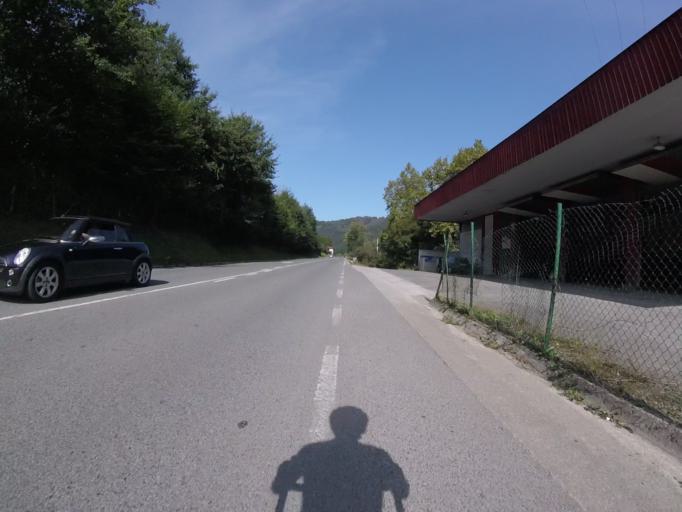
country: ES
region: Navarre
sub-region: Provincia de Navarra
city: Doneztebe
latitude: 43.1380
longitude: -1.5571
